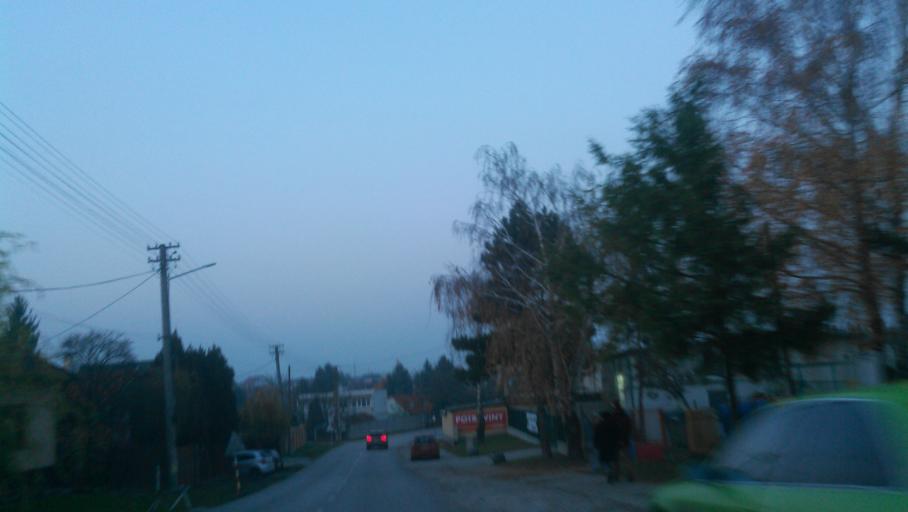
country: SK
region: Bratislavsky
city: Modra
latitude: 48.3007
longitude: 17.3396
